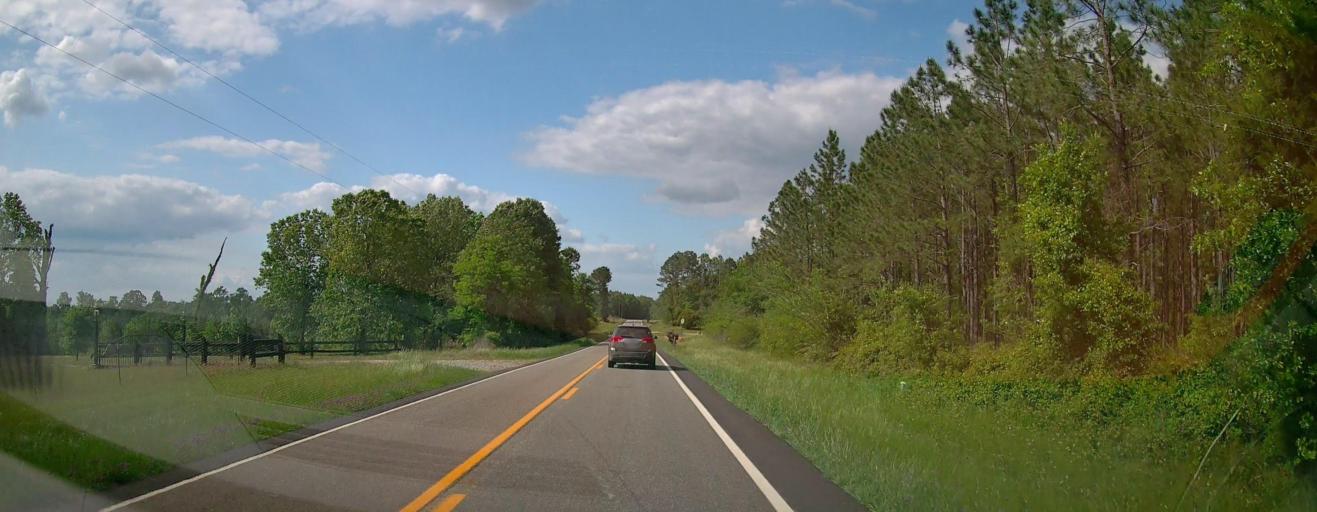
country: US
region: Georgia
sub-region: Laurens County
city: East Dublin
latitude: 32.6458
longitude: -82.8954
